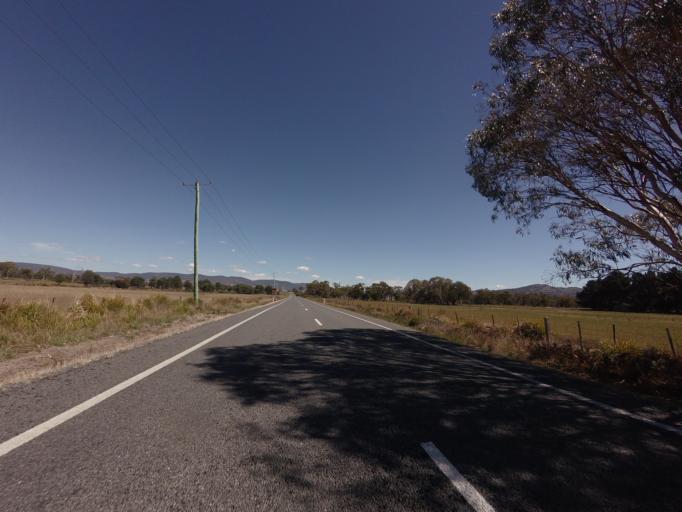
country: AU
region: Tasmania
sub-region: Northern Midlands
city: Evandale
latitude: -41.7657
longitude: 147.7450
